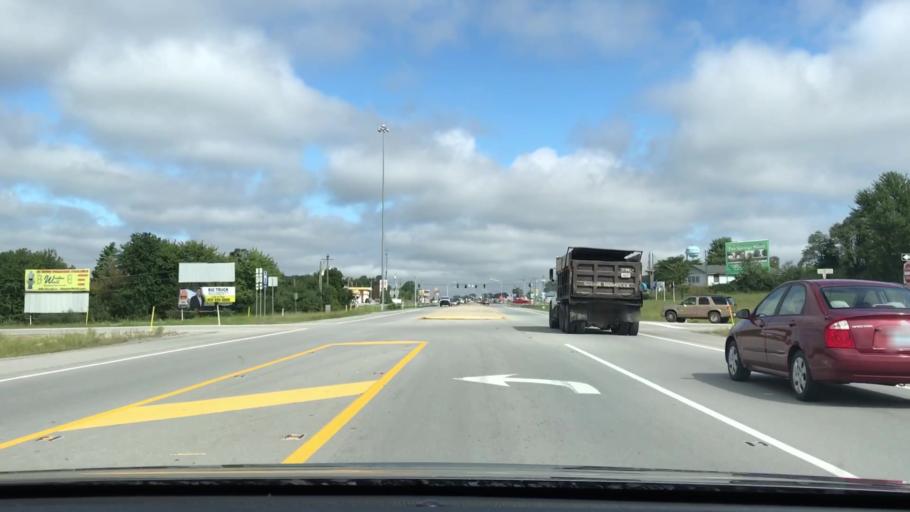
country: US
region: Kentucky
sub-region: Russell County
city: Russell Springs
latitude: 37.0527
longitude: -85.0702
